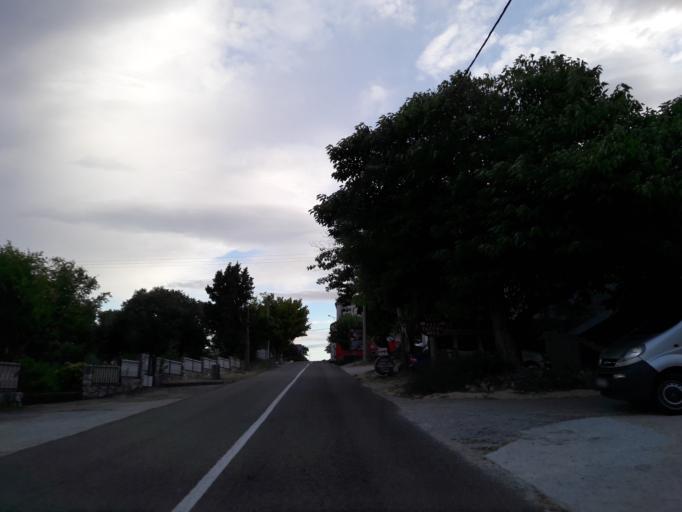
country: HR
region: Dubrovacko-Neretvanska
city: Komin
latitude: 42.9255
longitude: 17.4313
